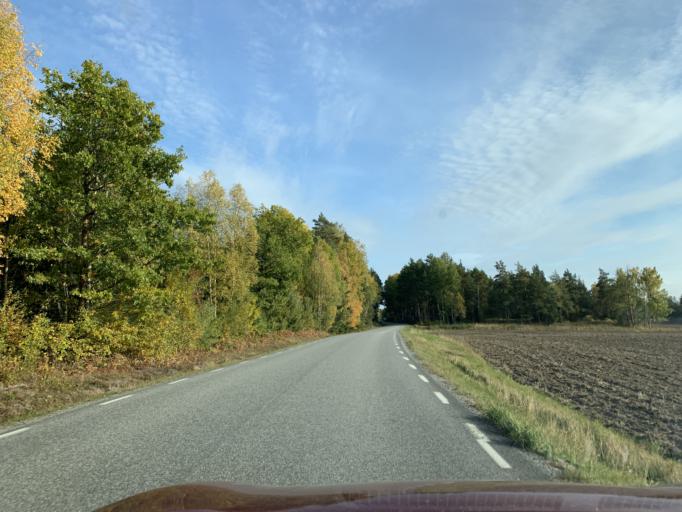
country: SE
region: Stockholm
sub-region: Upplands-Bro Kommun
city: Bro
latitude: 59.5075
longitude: 17.6028
